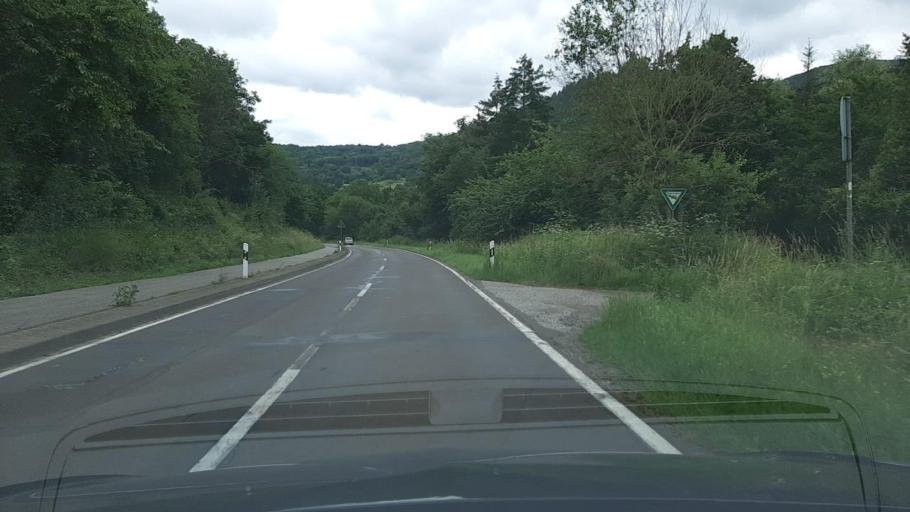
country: DE
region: Rheinland-Pfalz
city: Kamp-Bornhofen
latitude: 50.2060
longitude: 7.6148
